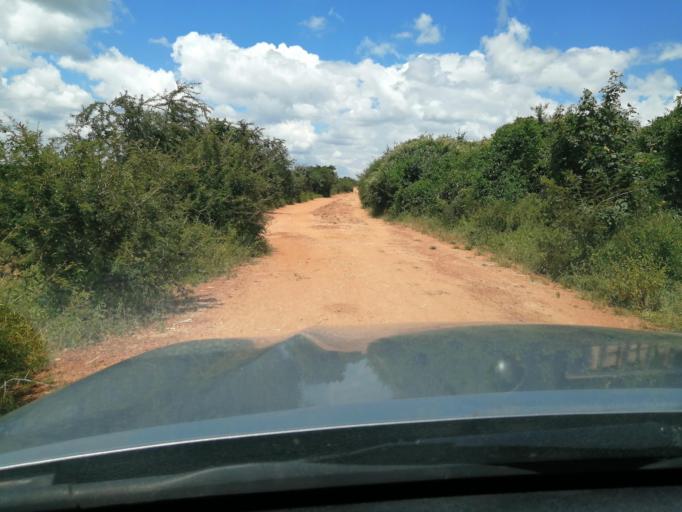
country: ZM
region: Lusaka
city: Lusaka
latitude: -15.1838
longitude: 27.9486
